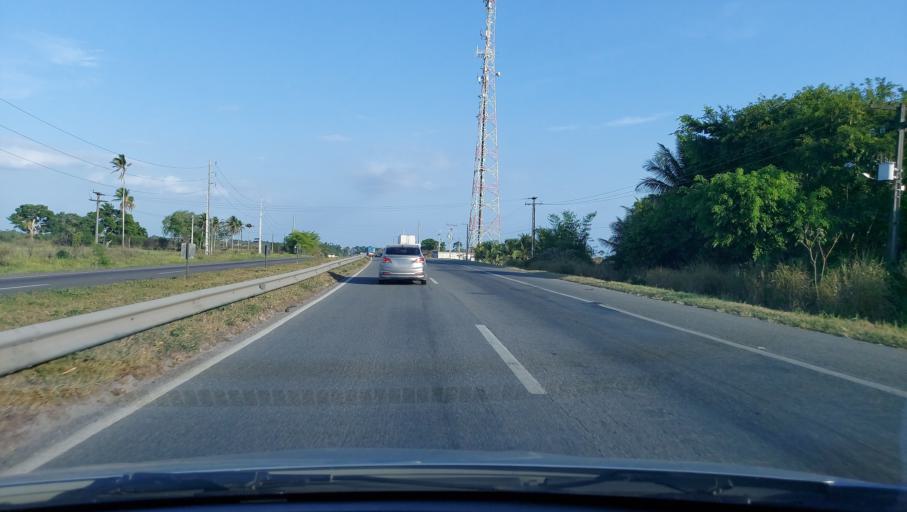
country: BR
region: Bahia
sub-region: Conceicao Do Jacuipe
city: Conceicao do Jacuipe
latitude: -12.3895
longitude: -38.7866
